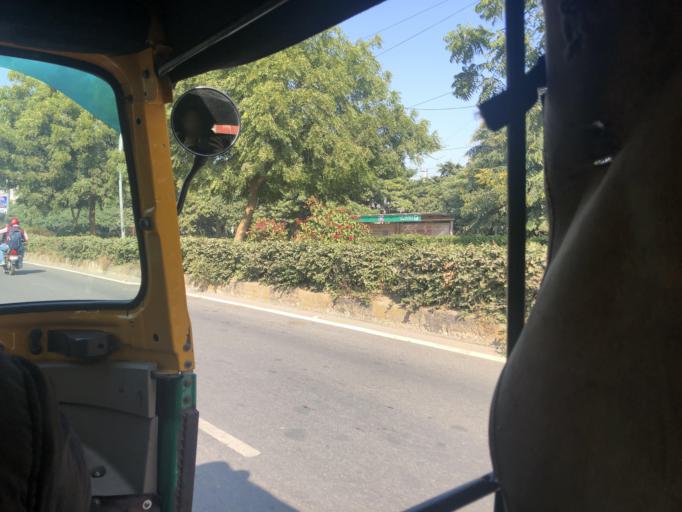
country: IN
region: Haryana
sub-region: Gurgaon
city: Gurgaon
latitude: 28.4455
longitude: 77.0815
